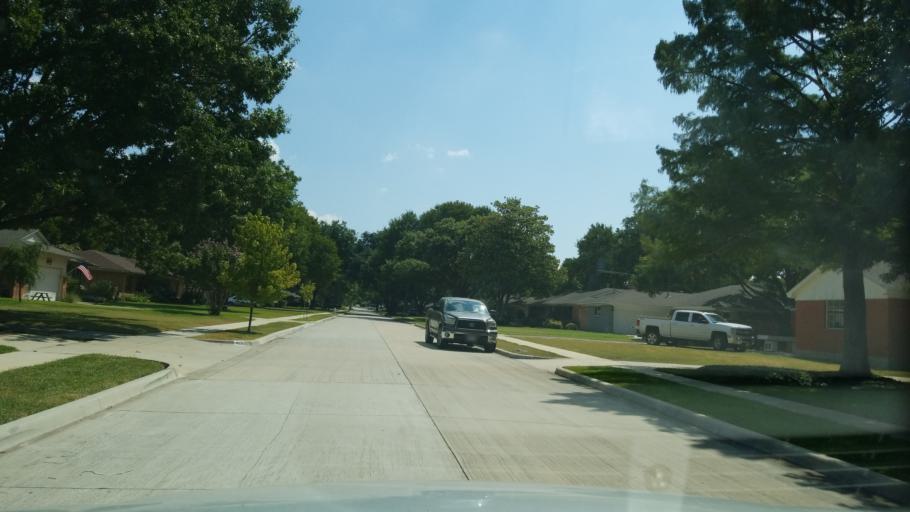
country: US
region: Texas
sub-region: Dallas County
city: Richardson
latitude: 32.9550
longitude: -96.7491
